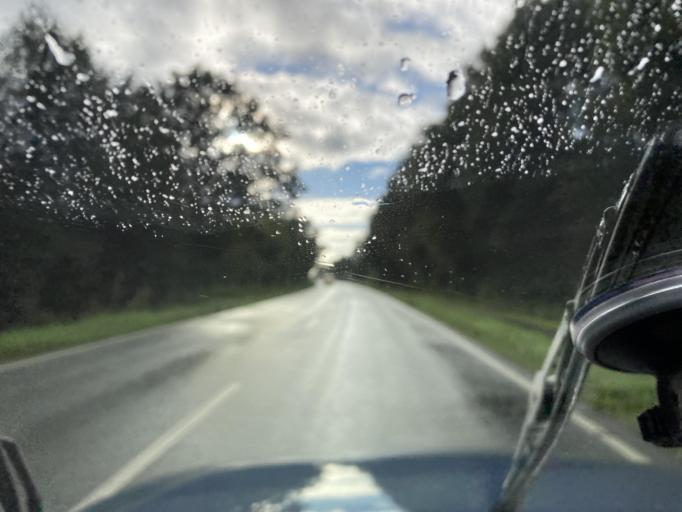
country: DE
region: Schleswig-Holstein
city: Tellingstedt
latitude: 54.2194
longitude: 9.3016
